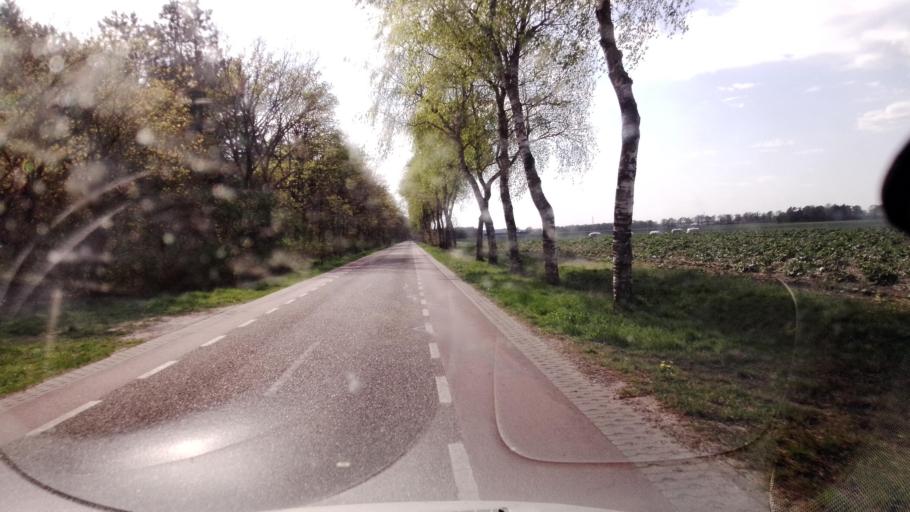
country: NL
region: Limburg
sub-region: Gemeente Venray
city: Venray
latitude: 51.4599
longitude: 5.9667
